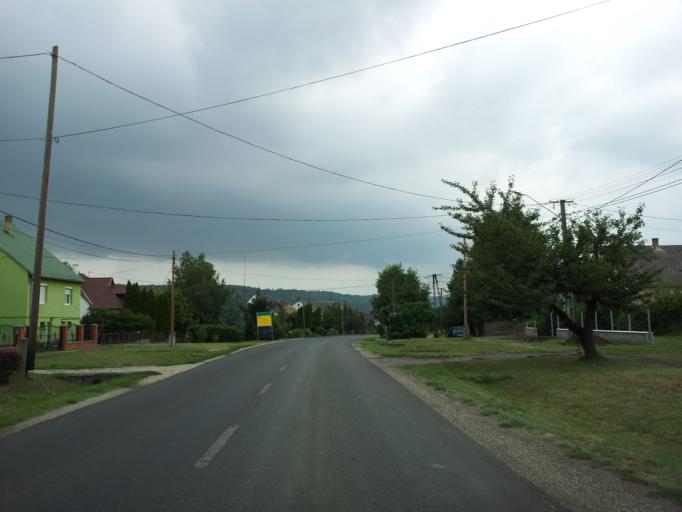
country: HU
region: Tolna
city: Hogyesz
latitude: 46.5265
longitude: 18.3741
